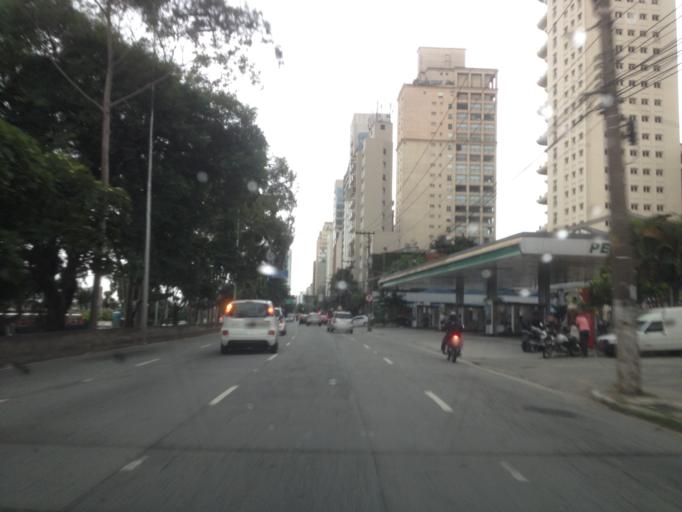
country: BR
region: Sao Paulo
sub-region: Sao Paulo
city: Sao Paulo
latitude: -23.5843
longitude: -46.6910
